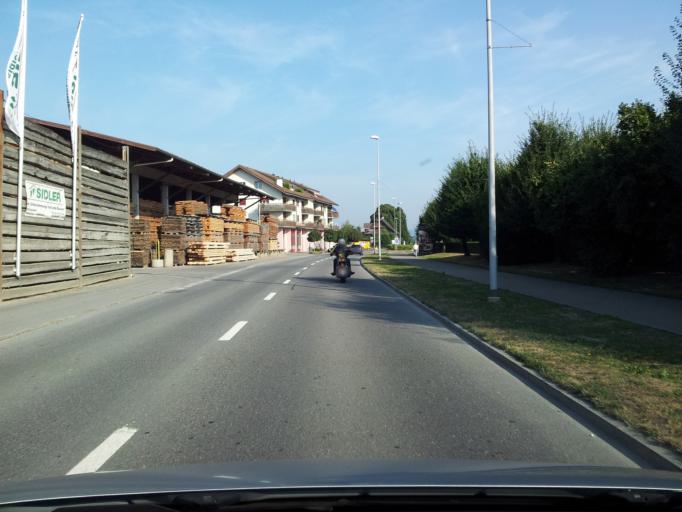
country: CH
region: Lucerne
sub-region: Sursee District
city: Nottwil
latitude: 47.1395
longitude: 8.1287
